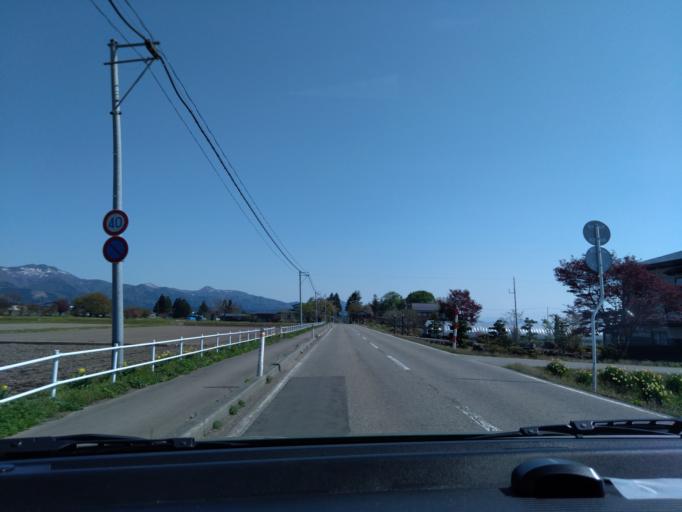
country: JP
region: Akita
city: Kakunodatemachi
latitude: 39.5261
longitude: 140.5870
